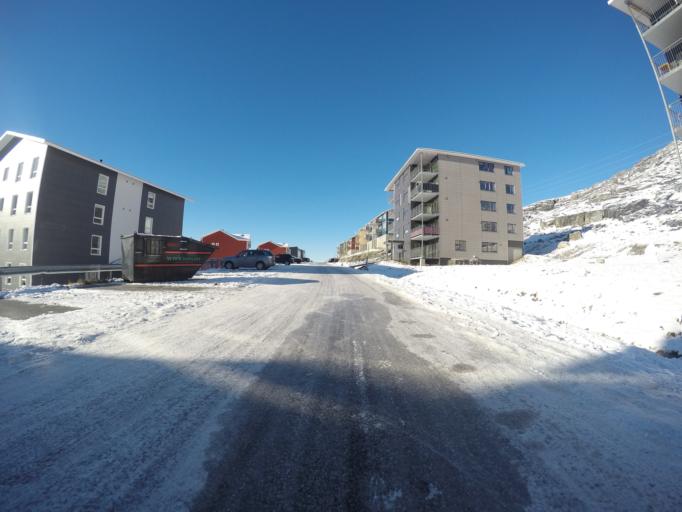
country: GL
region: Sermersooq
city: Nuuk
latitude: 64.1756
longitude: -51.6696
